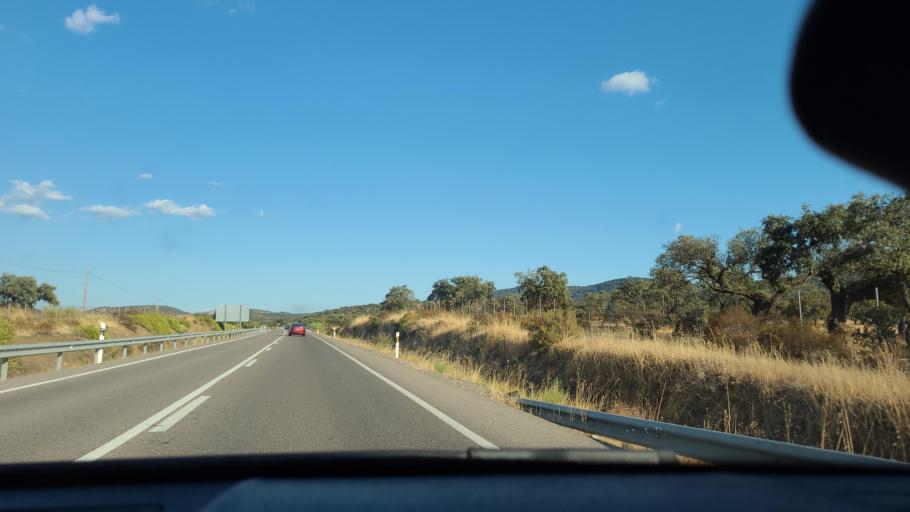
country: ES
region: Andalusia
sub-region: Province of Cordoba
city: Belmez
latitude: 38.2102
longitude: -5.1342
